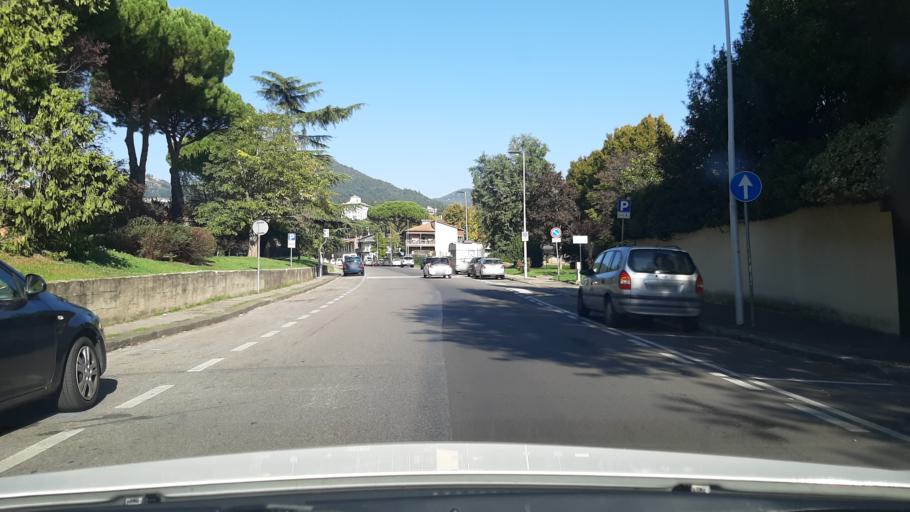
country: IT
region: Tuscany
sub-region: Province of Florence
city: Fiesole
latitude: 43.7816
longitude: 11.2932
